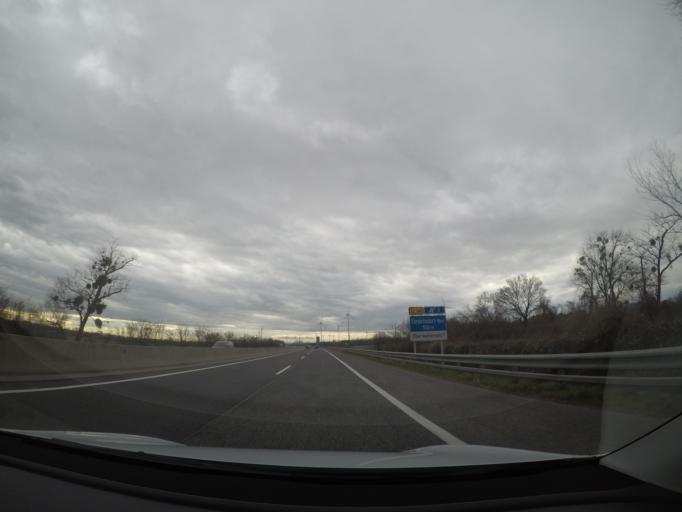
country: AT
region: Lower Austria
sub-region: Politischer Bezirk Baden
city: Trumau
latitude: 47.9704
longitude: 16.3680
